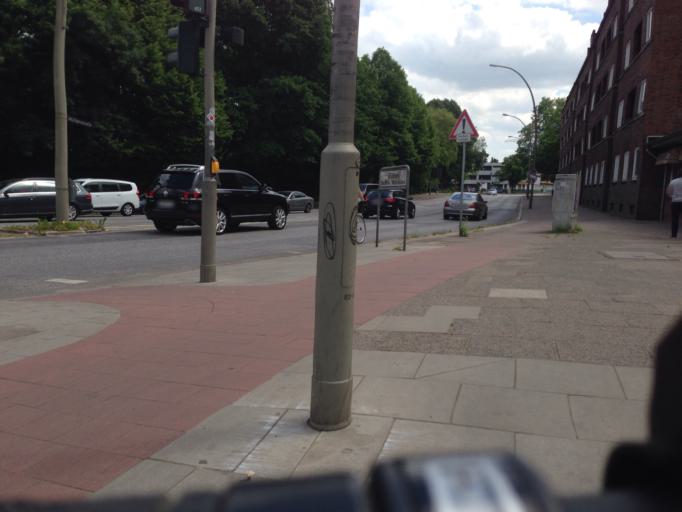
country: DE
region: Hamburg
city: Marienthal
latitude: 53.5760
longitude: 10.0581
